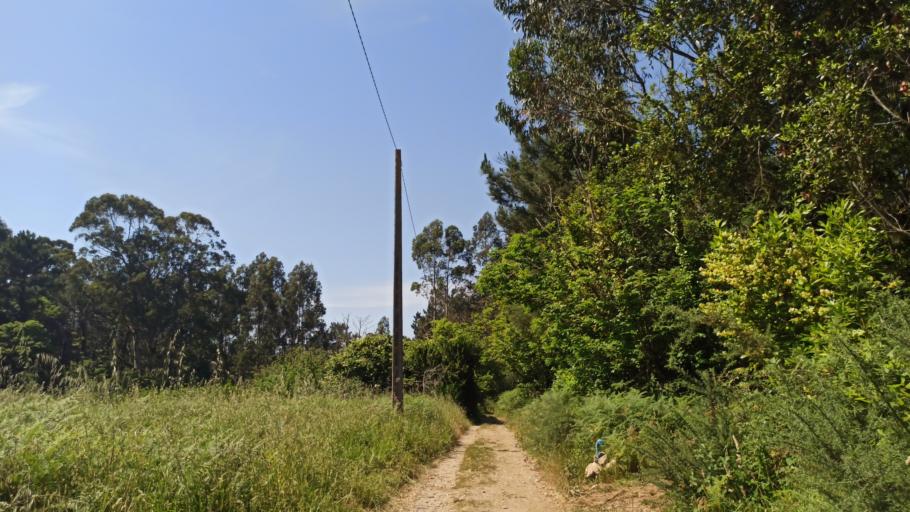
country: ES
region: Galicia
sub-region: Provincia da Coruna
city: Sada
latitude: 43.3793
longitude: -8.2701
